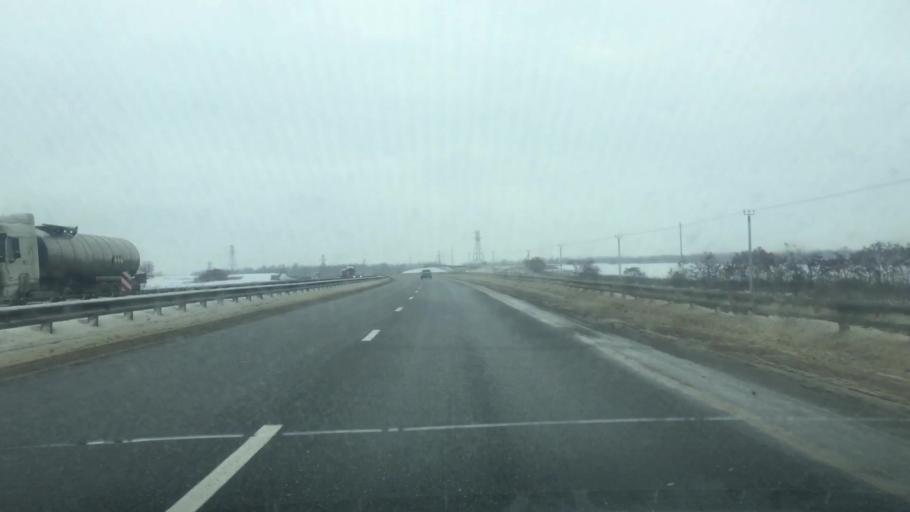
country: RU
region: Tula
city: Yefremov
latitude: 53.1025
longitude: 38.1784
